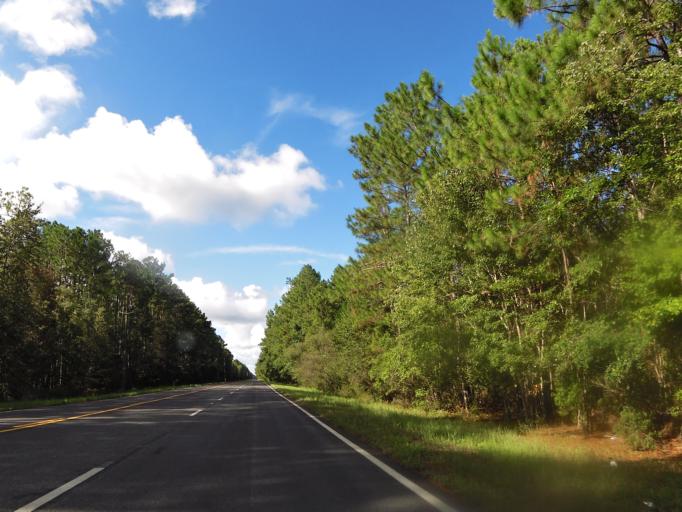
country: US
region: Georgia
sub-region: Camden County
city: Woodbine
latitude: 31.0116
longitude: -81.7315
